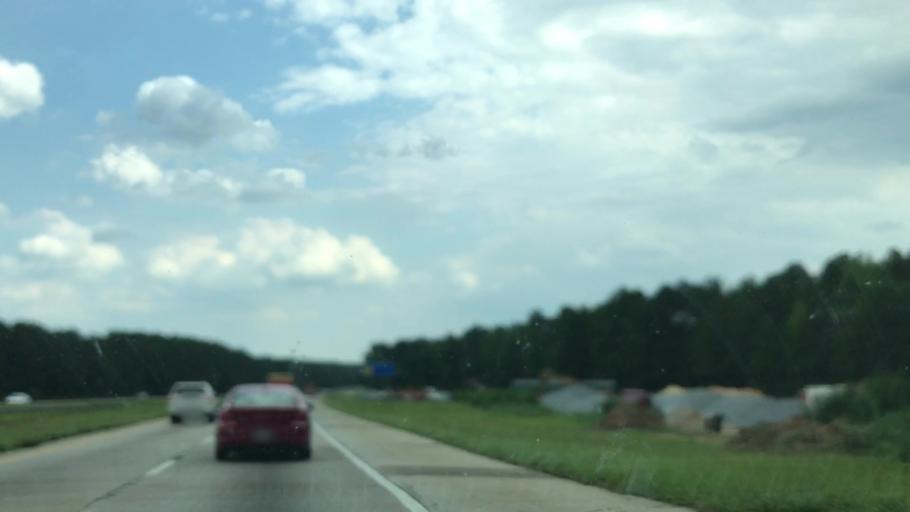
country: US
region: South Carolina
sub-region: Richland County
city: Blythewood
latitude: 34.3076
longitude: -81.0001
